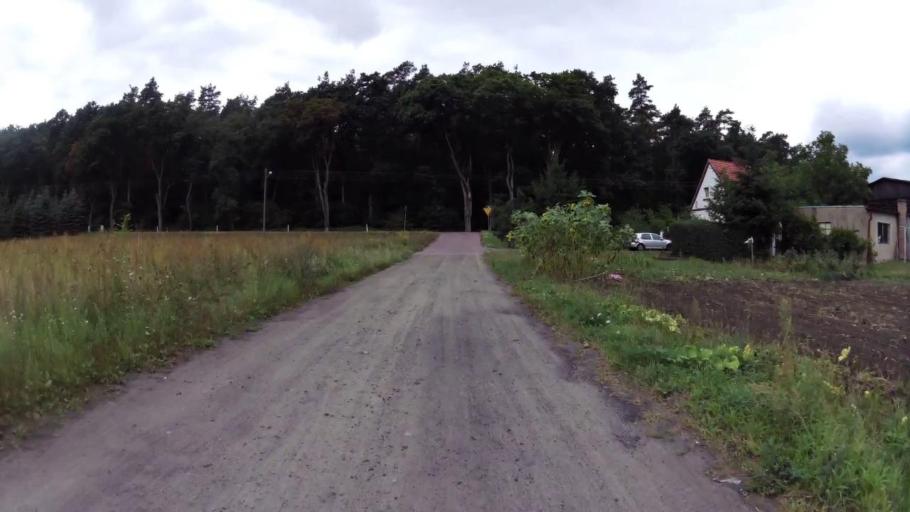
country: PL
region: West Pomeranian Voivodeship
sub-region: Powiat mysliborski
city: Debno
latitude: 52.7578
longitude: 14.6973
